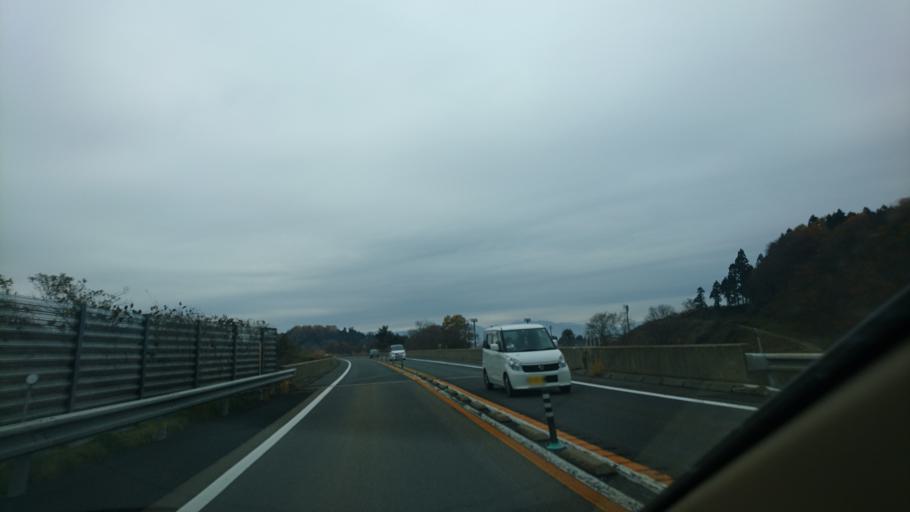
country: JP
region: Iwate
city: Kitakami
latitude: 39.2784
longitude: 141.0450
